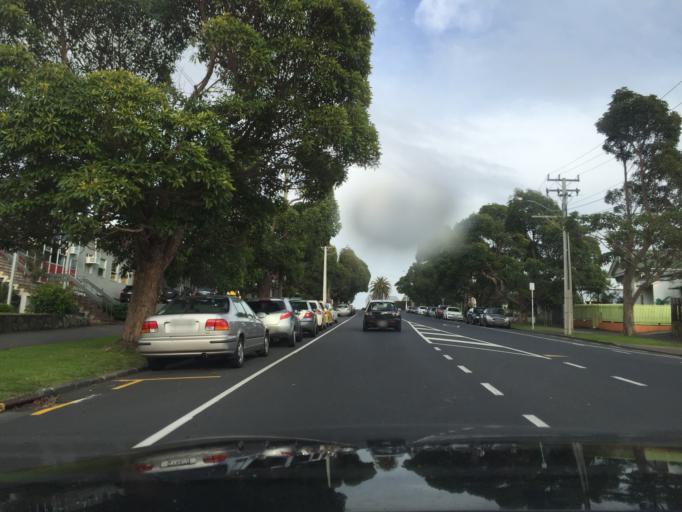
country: NZ
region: Auckland
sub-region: Auckland
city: Auckland
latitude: -36.8547
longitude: 174.7316
